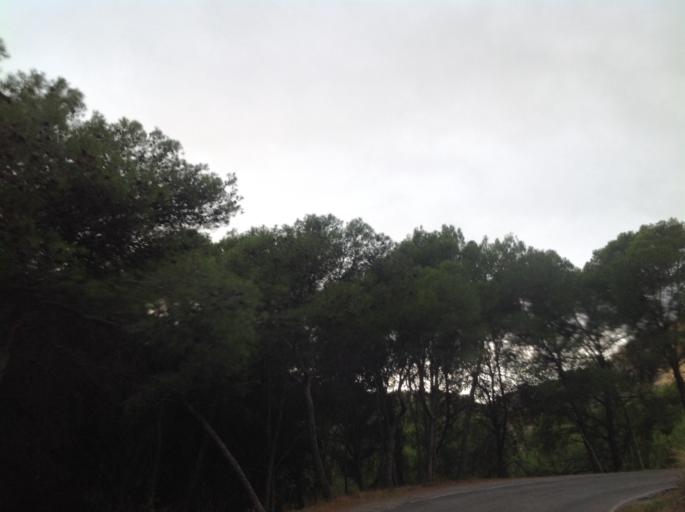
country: ES
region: Andalusia
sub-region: Provincia de Malaga
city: Carratraca
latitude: 36.9110
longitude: -4.7865
